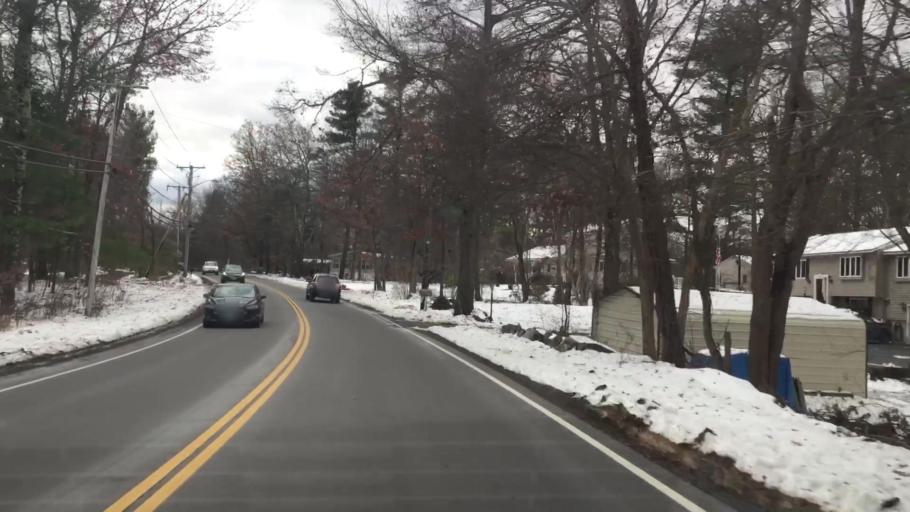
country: US
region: New Hampshire
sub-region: Rockingham County
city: Windham
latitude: 42.7580
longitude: -71.2648
